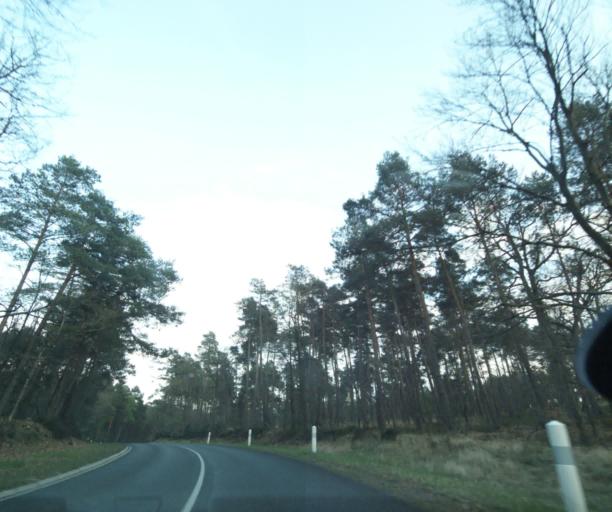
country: FR
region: Ile-de-France
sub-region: Departement de Seine-et-Marne
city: Montigny-sur-Loing
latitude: 48.3694
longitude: 2.7589
